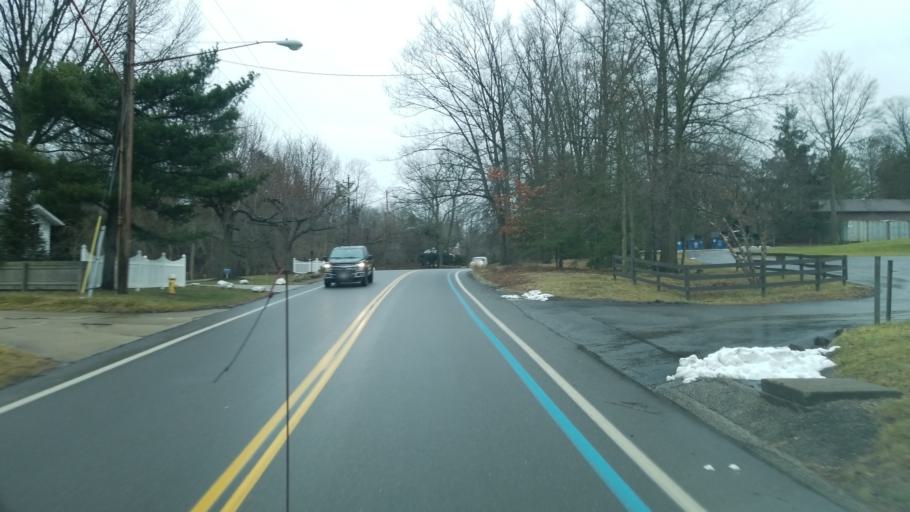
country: US
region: Ohio
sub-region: Summit County
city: Akron
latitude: 41.1228
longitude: -81.5485
